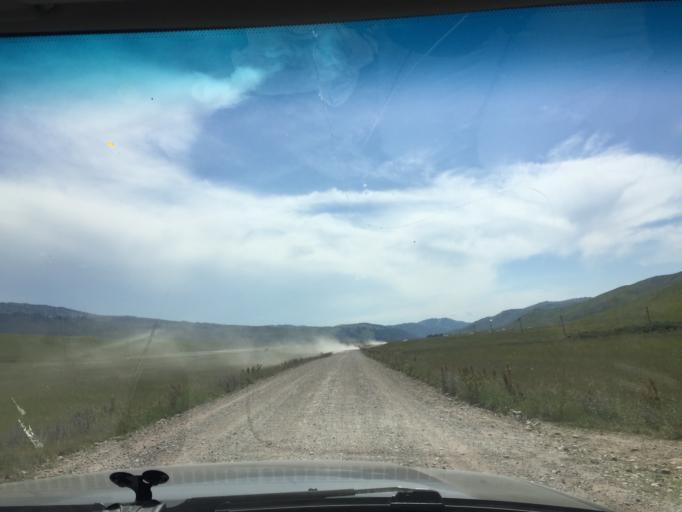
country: KZ
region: Almaty Oblysy
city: Kegen
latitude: 42.7587
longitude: 79.0204
